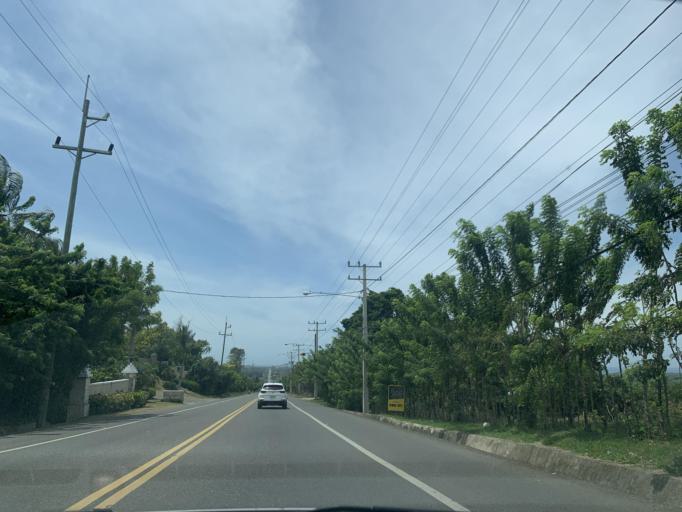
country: DO
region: Puerto Plata
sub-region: Puerto Plata
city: Puerto Plata
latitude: 19.7298
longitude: -70.6258
